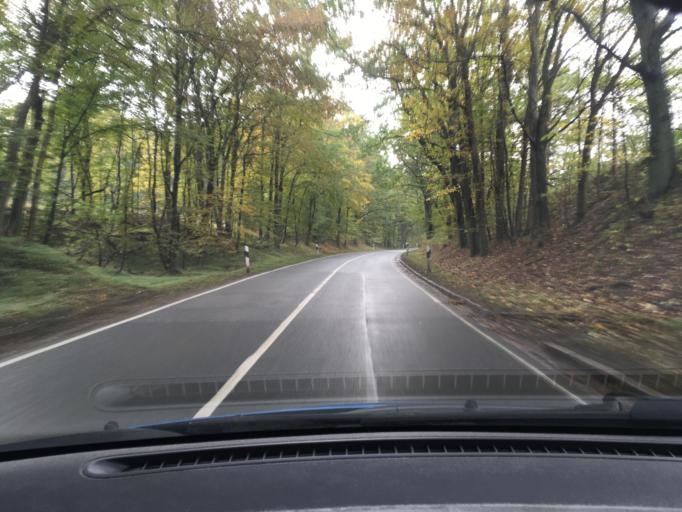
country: DE
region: Schleswig-Holstein
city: Damsdorf
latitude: 54.0599
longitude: 10.3261
